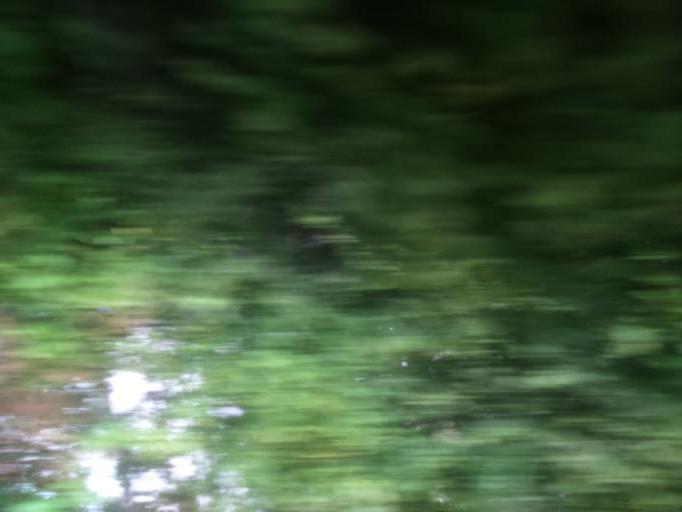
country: FR
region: Rhone-Alpes
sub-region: Departement de l'Isere
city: Le Pont-de-Claix
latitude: 45.1353
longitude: 5.7021
